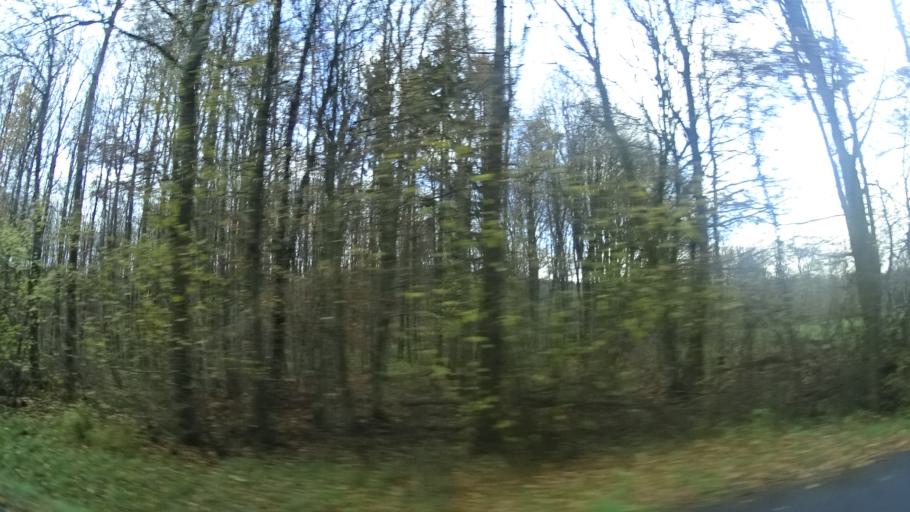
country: DE
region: Hesse
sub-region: Regierungsbezirk Kassel
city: Rasdorf
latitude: 50.7093
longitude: 9.8498
